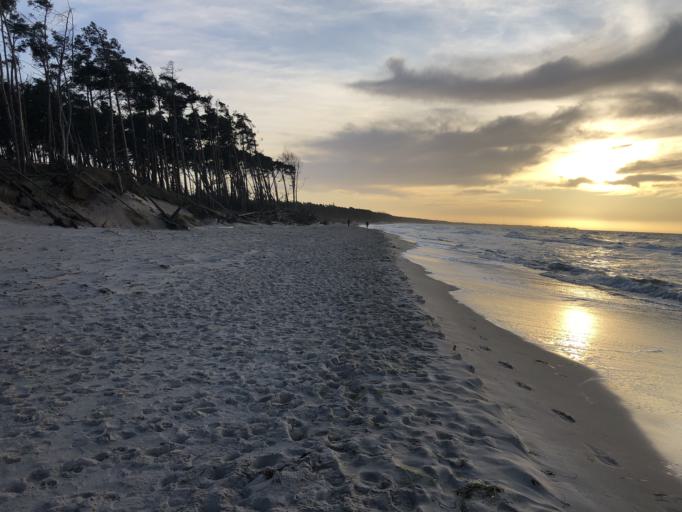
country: DE
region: Mecklenburg-Vorpommern
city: Born
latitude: 54.4351
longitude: 12.4754
